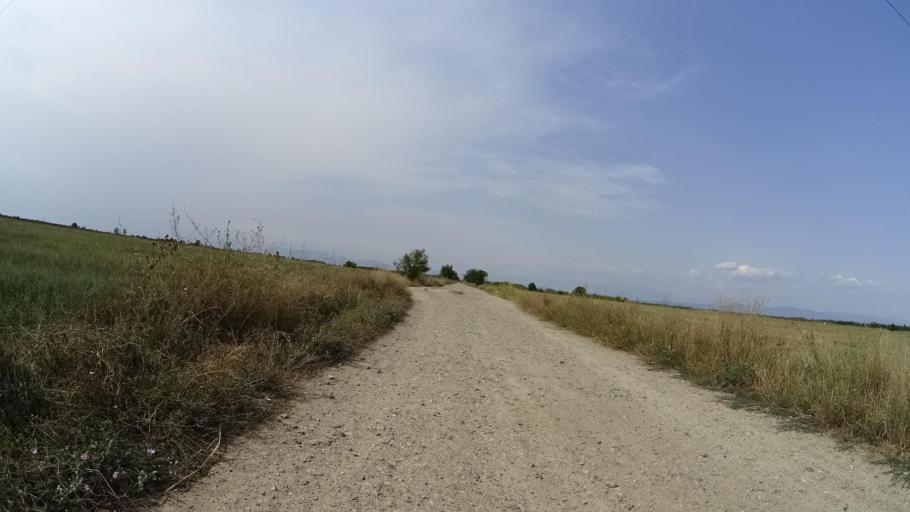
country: BG
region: Plovdiv
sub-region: Obshtina Kaloyanovo
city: Kaloyanovo
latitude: 42.2736
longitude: 24.8010
